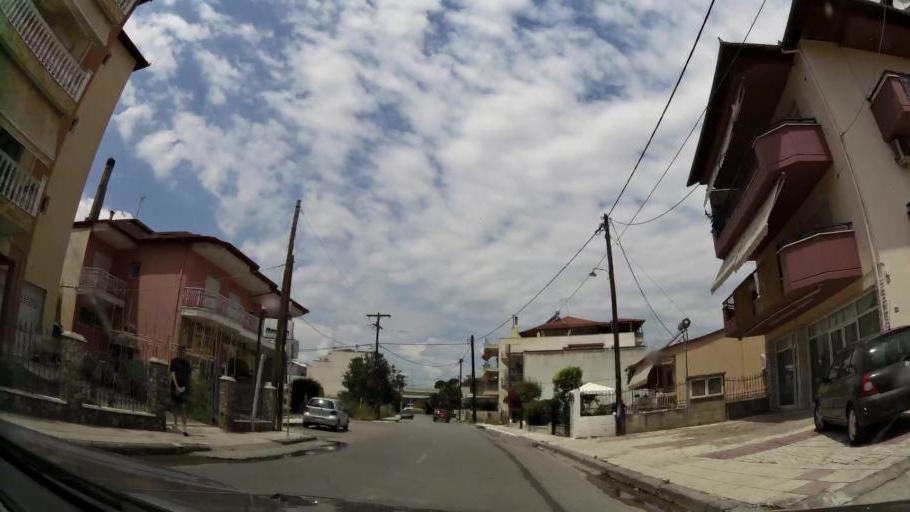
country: GR
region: Central Macedonia
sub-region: Nomos Pierias
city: Katerini
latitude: 40.2735
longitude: 22.5174
